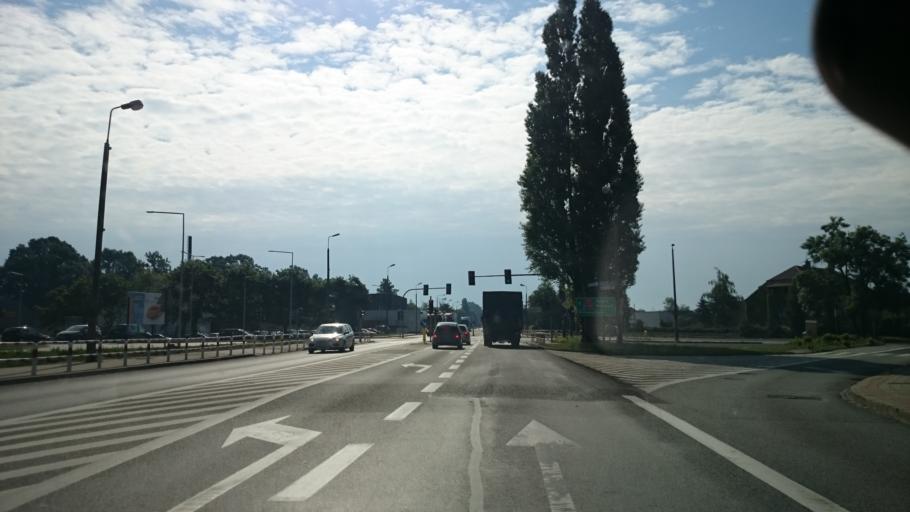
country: PL
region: Opole Voivodeship
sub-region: Powiat strzelecki
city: Strzelce Opolskie
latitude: 50.5074
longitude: 18.3111
